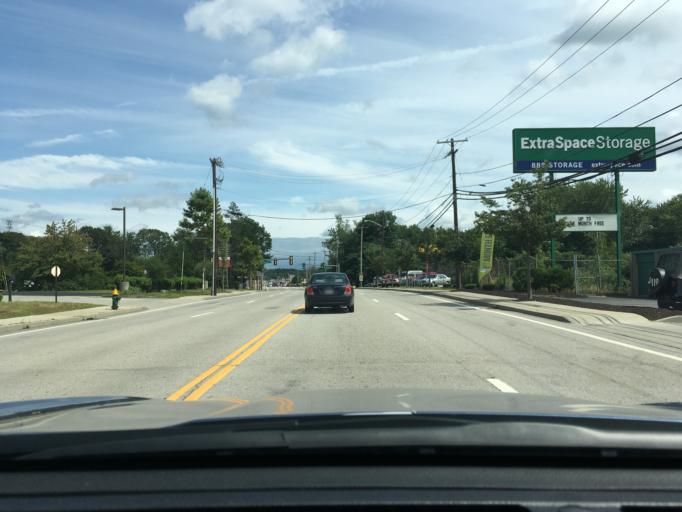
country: US
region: Rhode Island
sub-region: Providence County
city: Johnston
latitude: 41.8262
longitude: -71.5087
